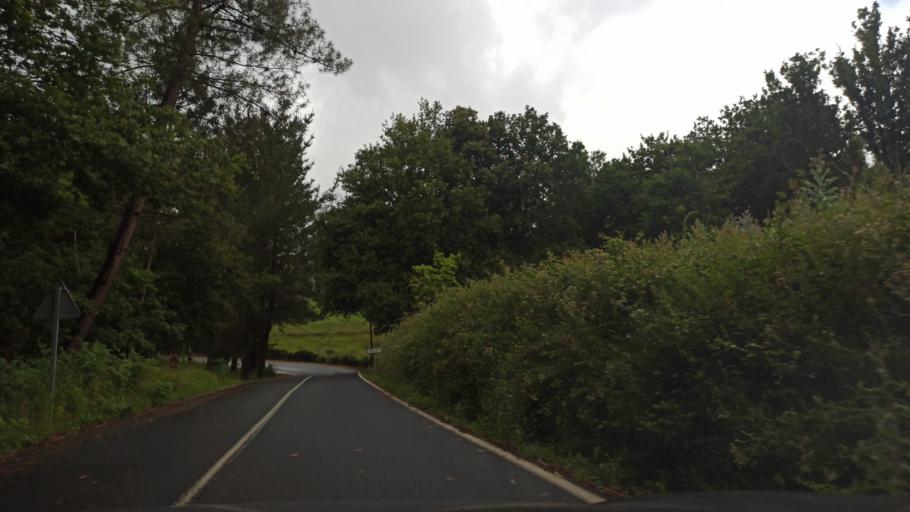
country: ES
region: Galicia
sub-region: Provincia da Coruna
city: Santiso
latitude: 42.7844
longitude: -8.0503
